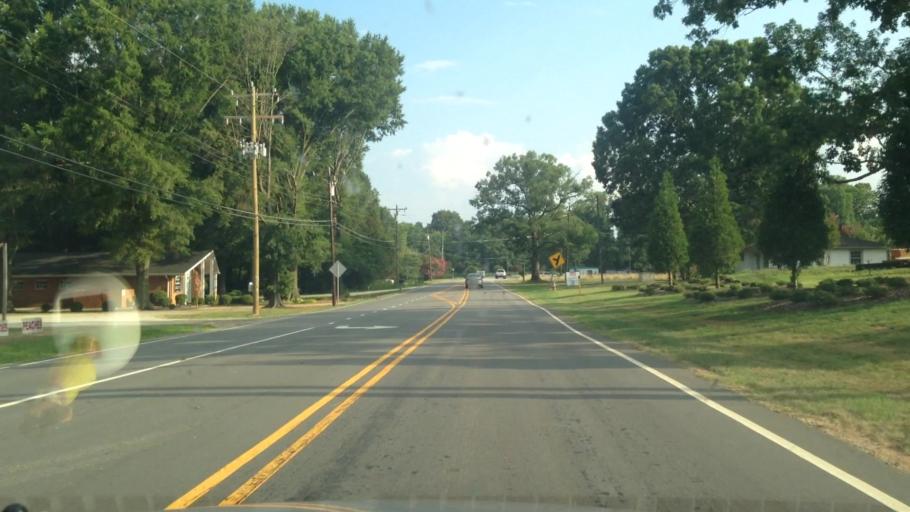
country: US
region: North Carolina
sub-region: Forsyth County
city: Kernersville
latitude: 36.0718
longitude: -80.0589
